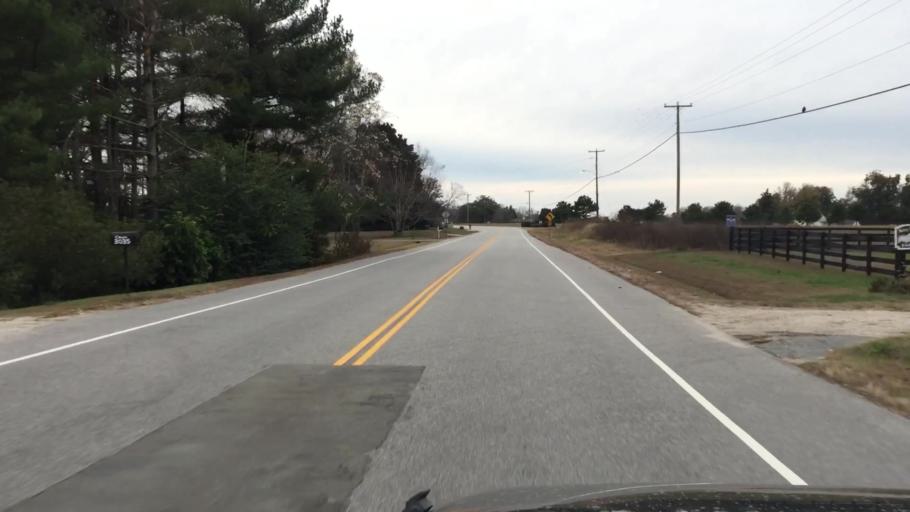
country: US
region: Virginia
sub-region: James City County
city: Williamsburg
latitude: 37.3824
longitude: -76.8100
